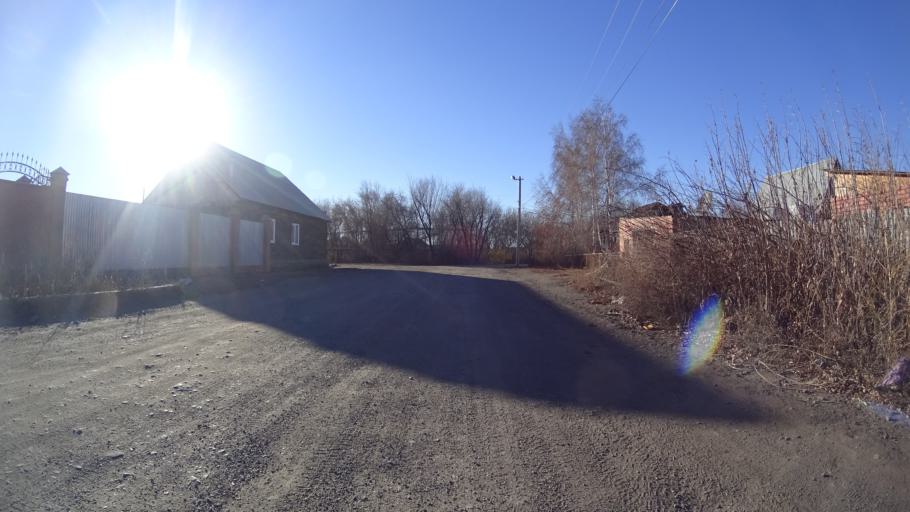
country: RU
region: Chelyabinsk
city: Troitsk
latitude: 54.1074
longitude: 61.5590
